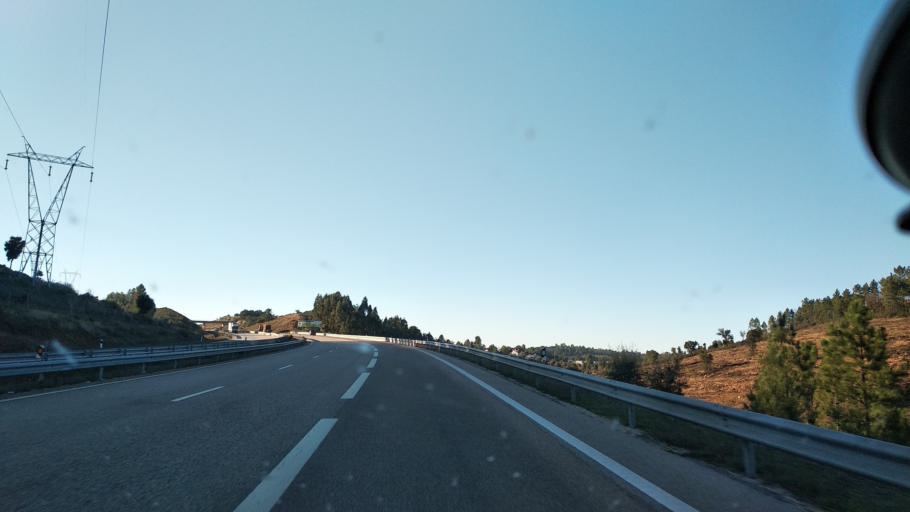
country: PT
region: Santarem
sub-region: Abrantes
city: Alferrarede
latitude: 39.4950
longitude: -8.0738
